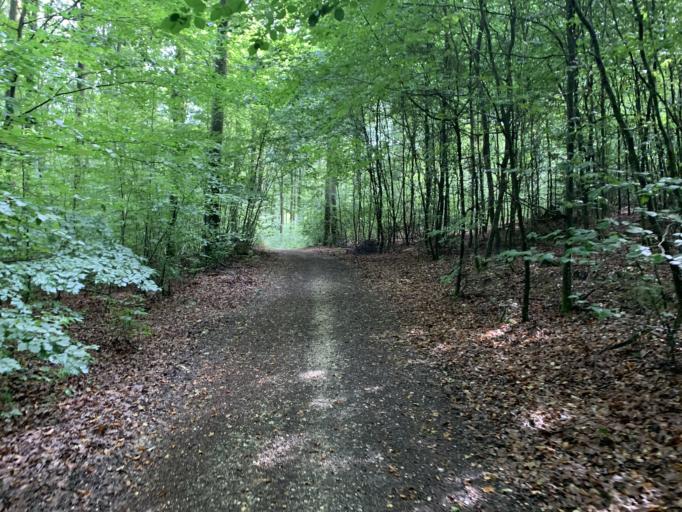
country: DE
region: Rheinland-Pfalz
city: Rettert
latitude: 50.2145
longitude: 7.9422
